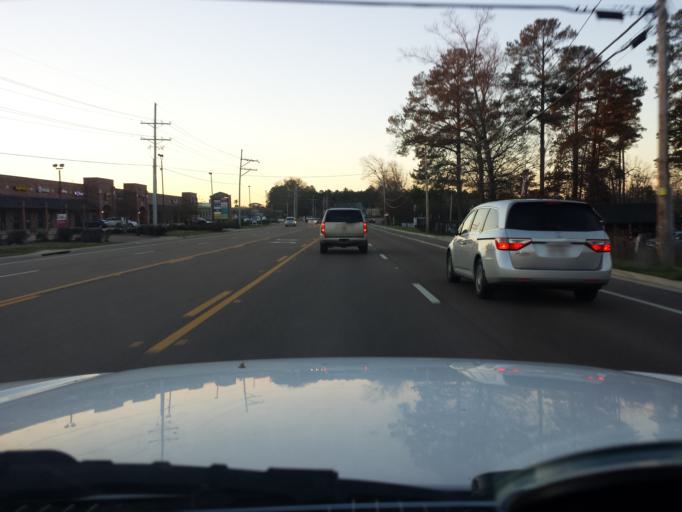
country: US
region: Mississippi
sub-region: Madison County
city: Ridgeland
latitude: 32.3813
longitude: -90.0427
